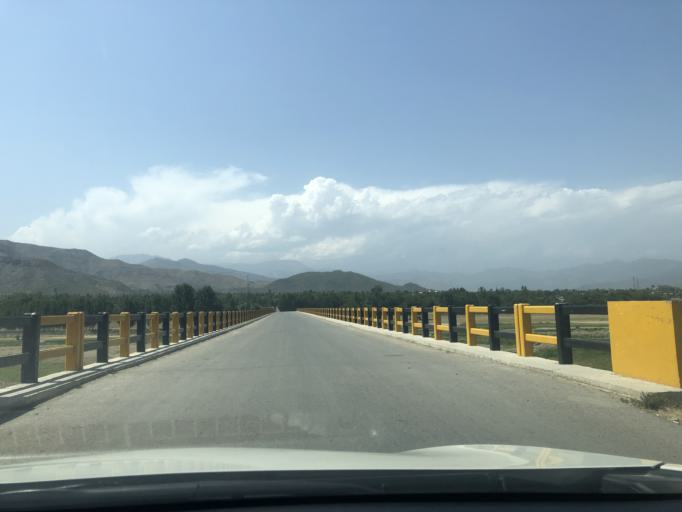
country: PK
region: Khyber Pakhtunkhwa
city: Timurgara
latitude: 34.7918
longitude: 71.6632
